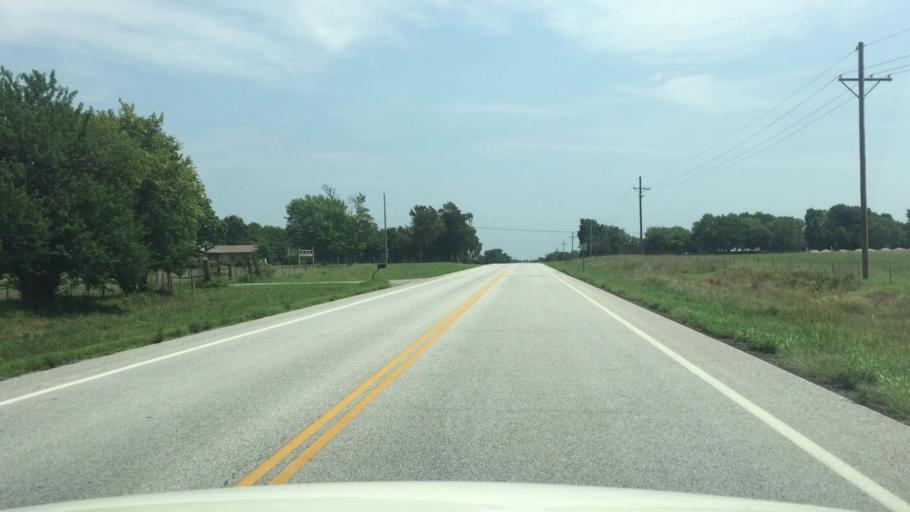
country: US
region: Kansas
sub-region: Cherokee County
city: Columbus
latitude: 37.1780
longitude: -94.7852
